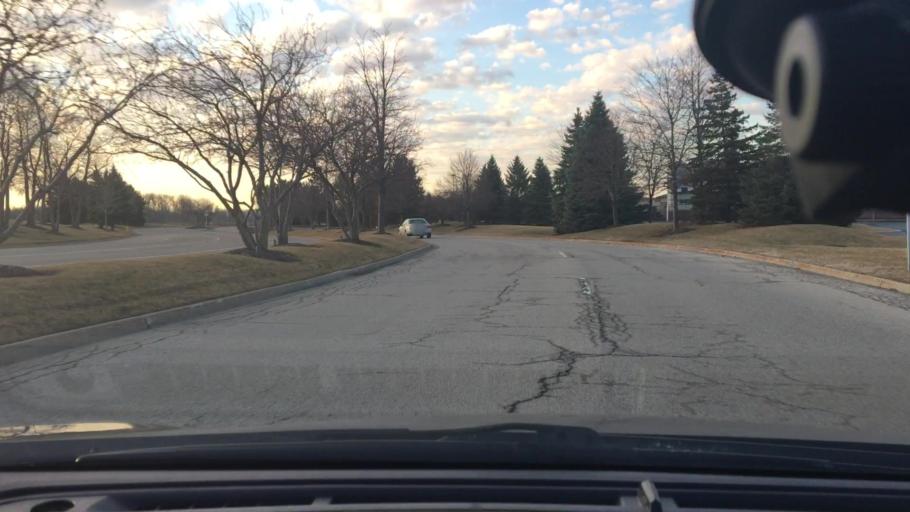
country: US
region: Illinois
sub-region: Cook County
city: Northbrook
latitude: 42.1051
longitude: -87.8114
